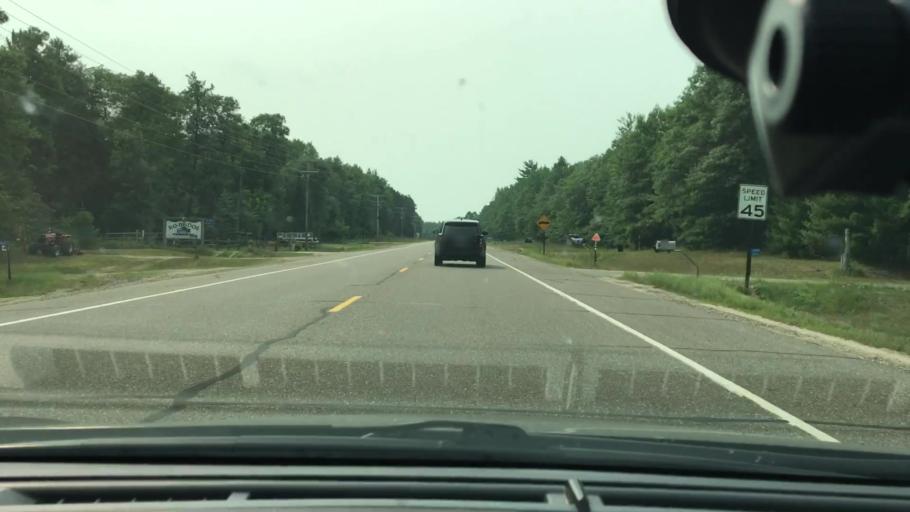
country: US
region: Minnesota
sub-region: Crow Wing County
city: Cross Lake
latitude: 46.5833
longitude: -94.1315
